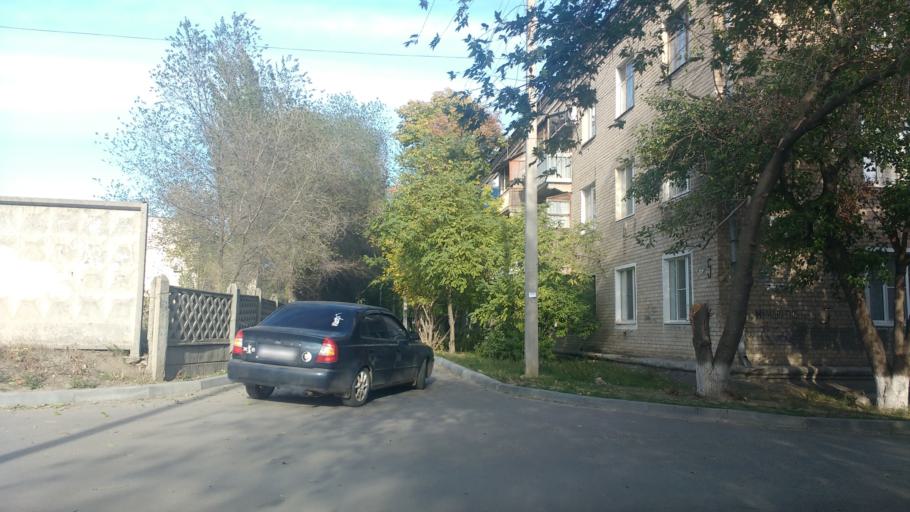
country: RU
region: Volgograd
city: Krasnoslobodsk
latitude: 48.7638
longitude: 44.5544
